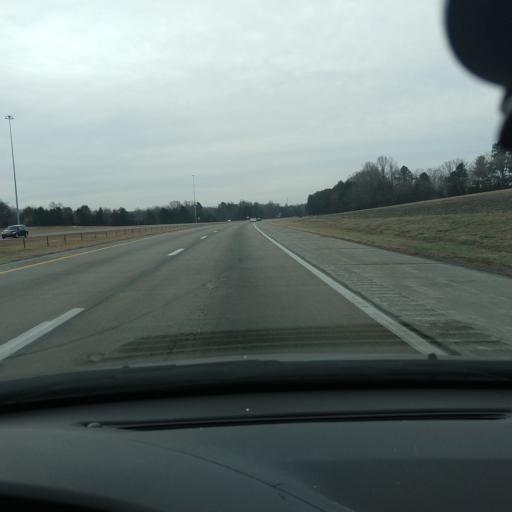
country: US
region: North Carolina
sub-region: Davidson County
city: Midway
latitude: 35.9701
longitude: -80.2300
